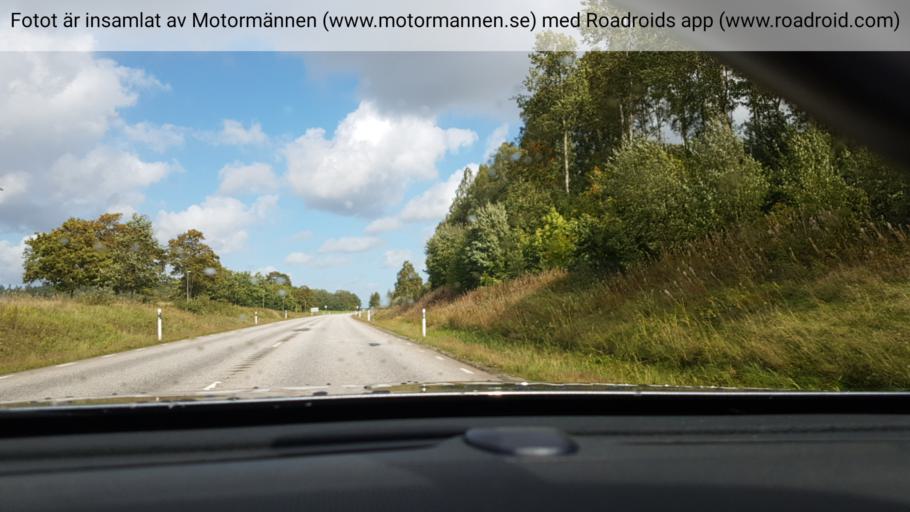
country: SE
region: Vaestra Goetaland
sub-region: Alingsas Kommun
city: Sollebrunn
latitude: 58.1014
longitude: 12.5107
